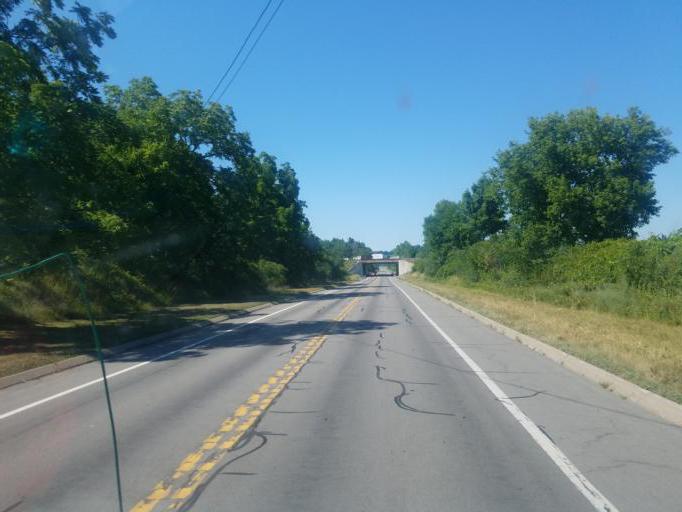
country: US
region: New York
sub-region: Ontario County
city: Phelps
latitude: 42.9679
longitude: -77.0758
